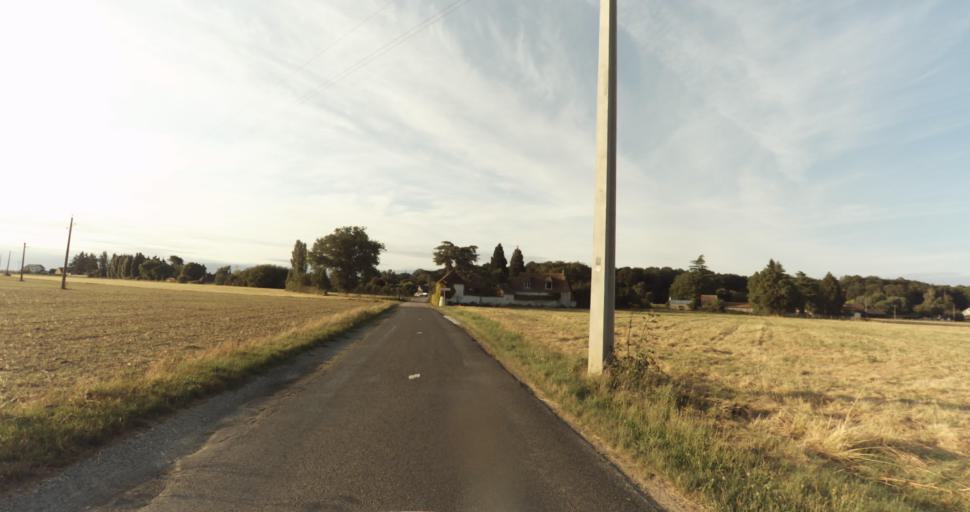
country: FR
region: Haute-Normandie
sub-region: Departement de l'Eure
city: Marcilly-sur-Eure
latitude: 48.8436
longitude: 1.2783
